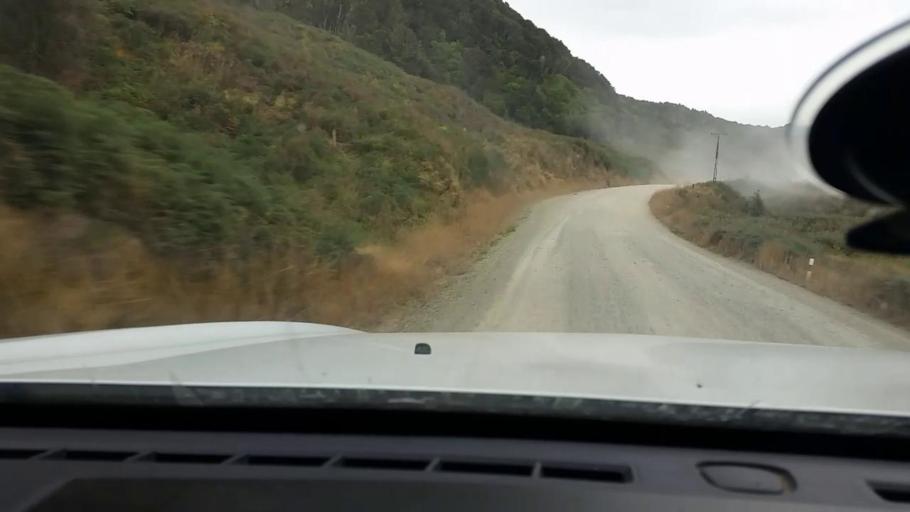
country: NZ
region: Otago
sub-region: Clutha District
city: Papatowai
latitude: -46.4687
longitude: 169.1322
